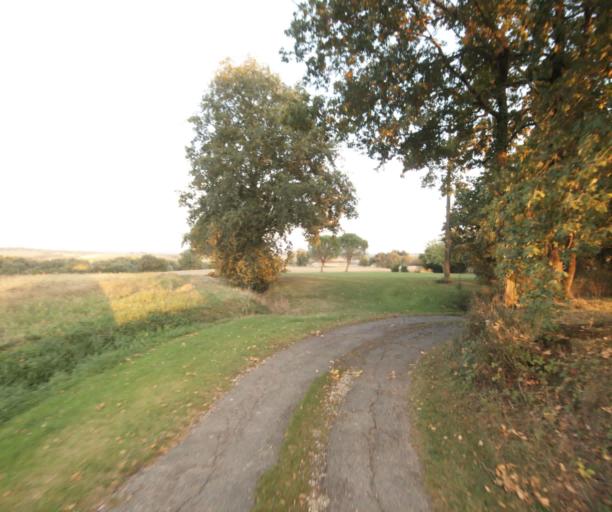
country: FR
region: Midi-Pyrenees
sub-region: Departement du Gers
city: Vic-Fezensac
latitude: 43.7831
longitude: 0.2434
